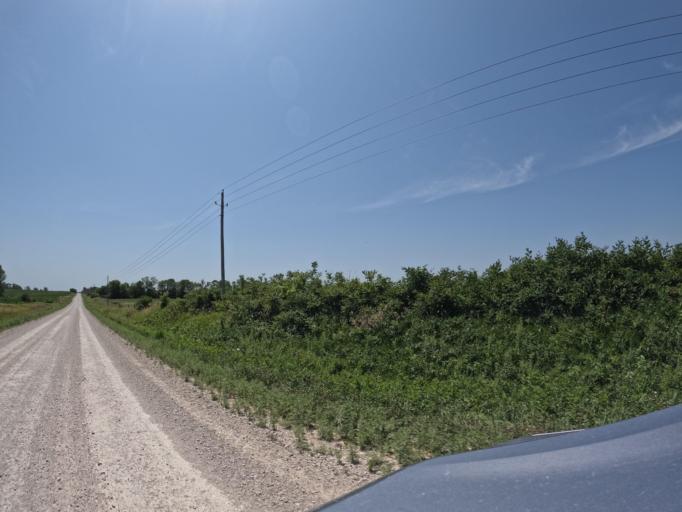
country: US
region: Iowa
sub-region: Henry County
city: Mount Pleasant
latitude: 40.9213
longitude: -91.6460
